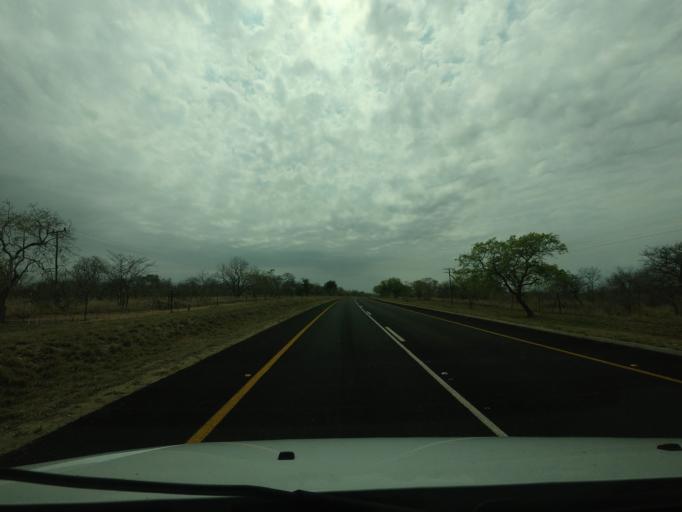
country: ZA
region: Limpopo
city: Thulamahashi
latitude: -24.5555
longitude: 31.1816
